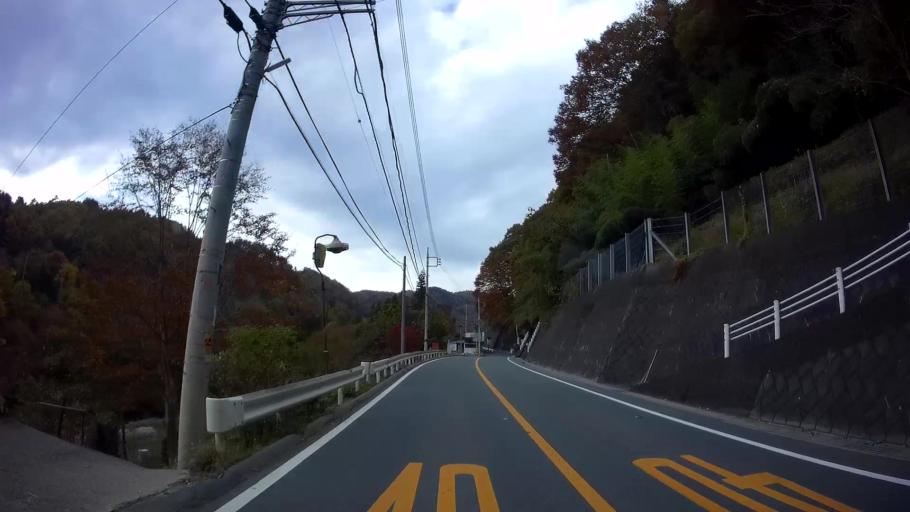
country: JP
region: Gunma
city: Nakanojomachi
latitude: 36.5683
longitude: 138.6369
